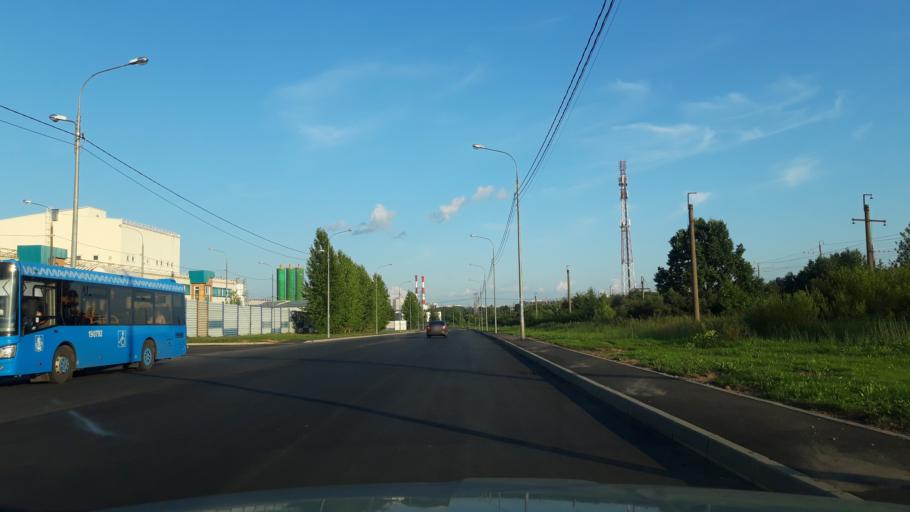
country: RU
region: Moskovskaya
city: Alabushevo
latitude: 56.0069
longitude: 37.1436
